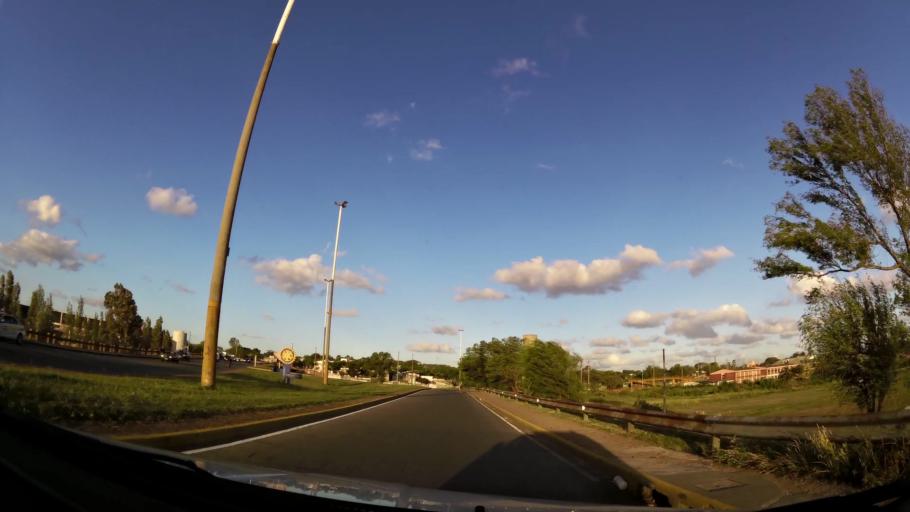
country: UY
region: Montevideo
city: Montevideo
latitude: -34.8723
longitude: -56.2431
